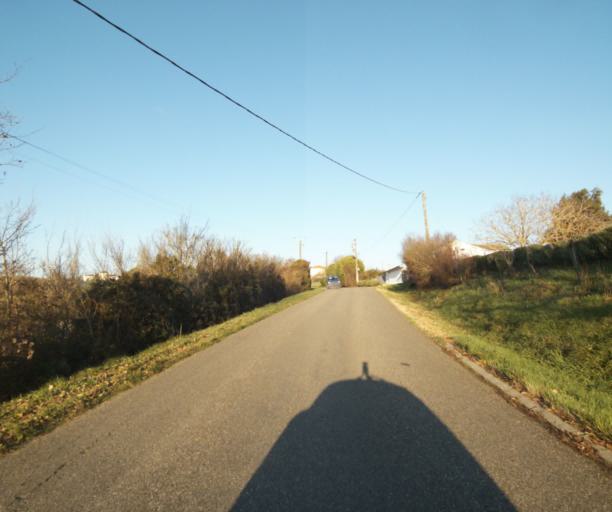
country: FR
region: Midi-Pyrenees
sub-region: Departement du Tarn-et-Garonne
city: Moissac
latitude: 44.1243
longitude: 1.1216
